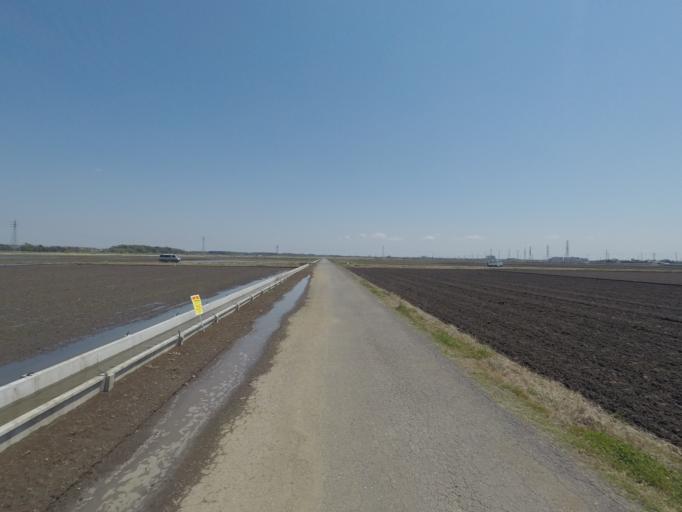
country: JP
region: Ibaraki
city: Fujishiro
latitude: 35.9482
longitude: 140.1047
